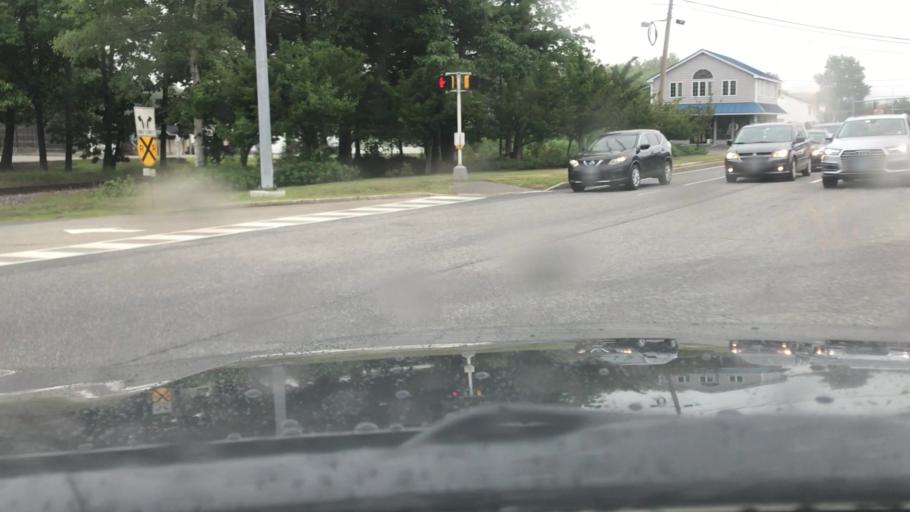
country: US
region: Maine
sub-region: Cumberland County
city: Brunswick
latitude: 43.9069
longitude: -69.9220
